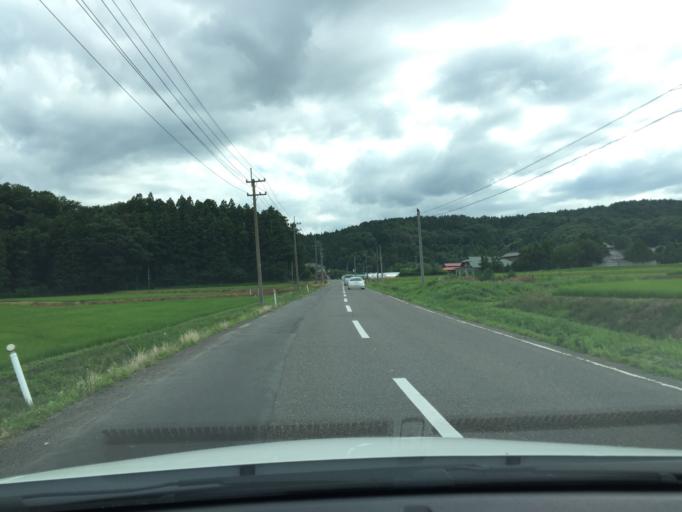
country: JP
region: Fukushima
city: Sukagawa
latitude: 37.3103
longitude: 140.2082
